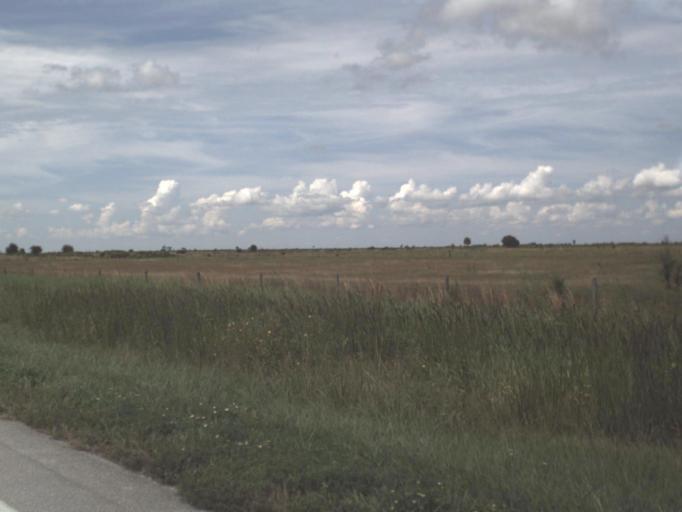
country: US
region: Florida
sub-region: Highlands County
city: Placid Lakes
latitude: 27.2092
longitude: -81.5371
